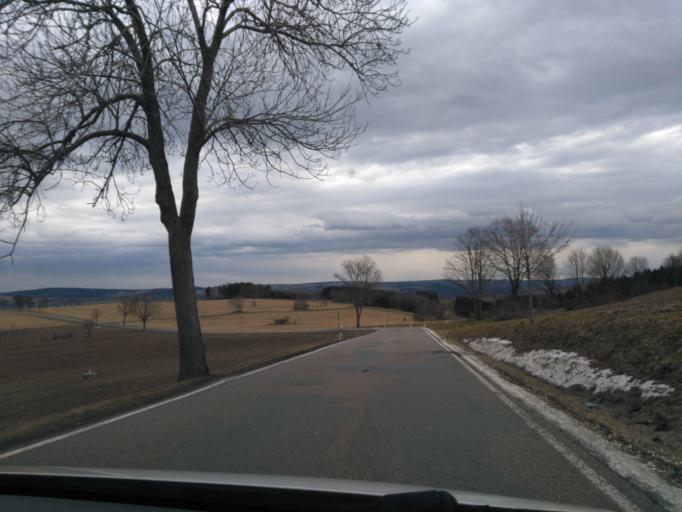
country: DE
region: Saxony
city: Drebach
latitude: 50.6415
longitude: 13.0166
